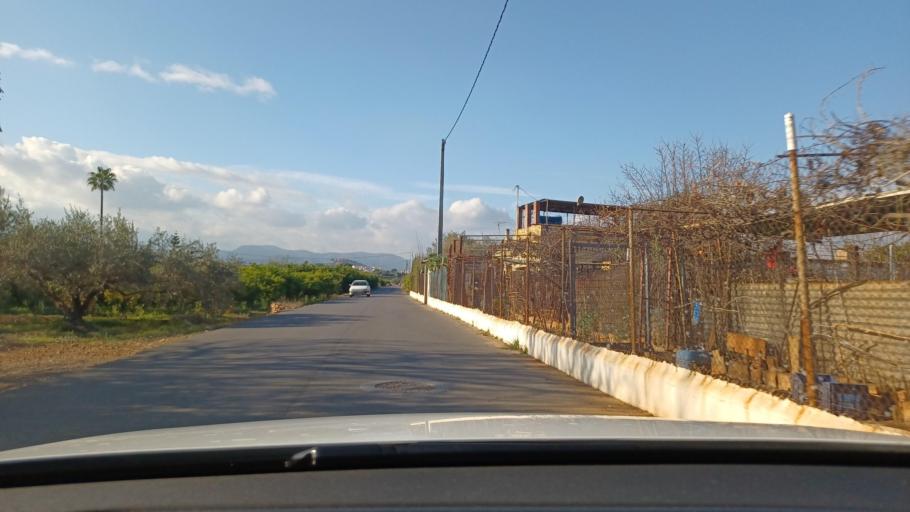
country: ES
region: Valencia
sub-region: Provincia de Castello
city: Onda
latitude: 39.9515
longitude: -0.2290
